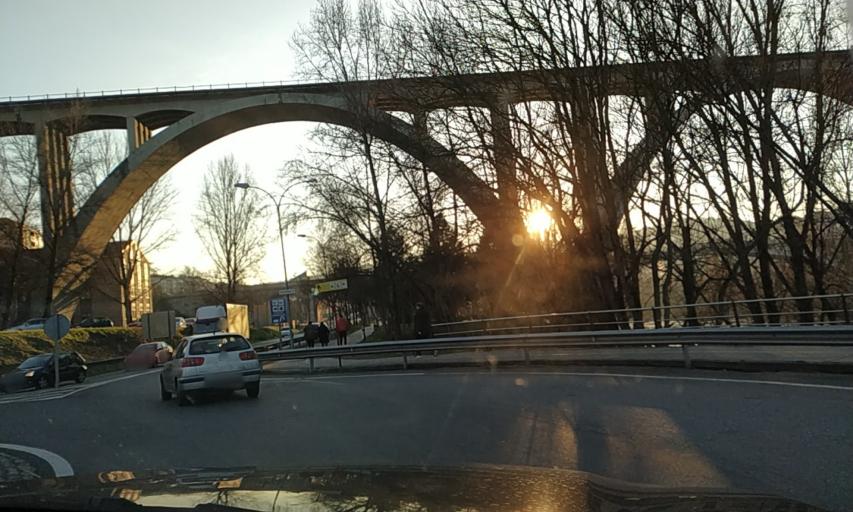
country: ES
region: Galicia
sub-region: Provincia de Ourense
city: Ourense
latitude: 42.3477
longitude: -7.8613
